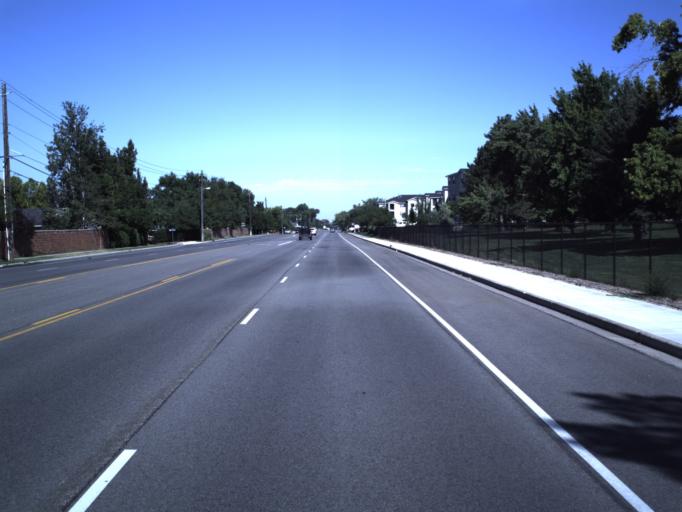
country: US
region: Utah
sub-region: Davis County
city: Fruit Heights
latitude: 41.0190
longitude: -111.9215
